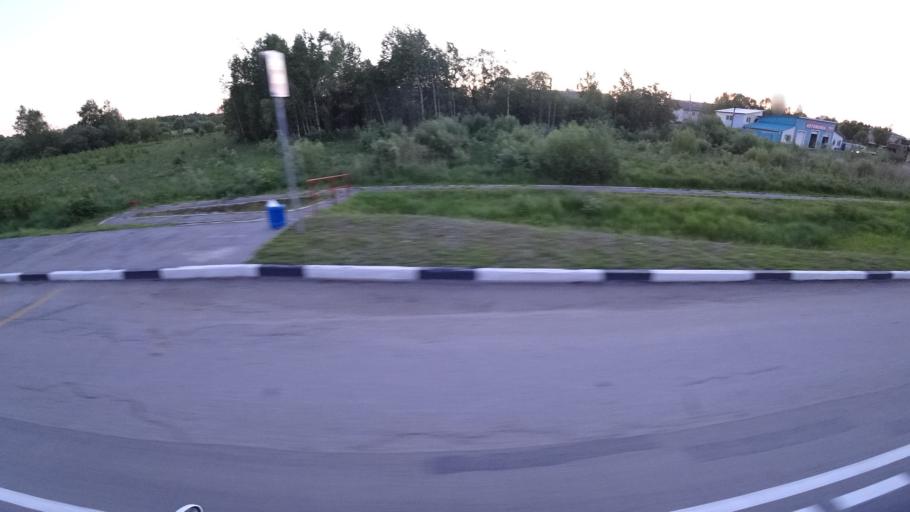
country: RU
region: Khabarovsk Krai
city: Khor
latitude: 47.8456
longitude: 134.9580
